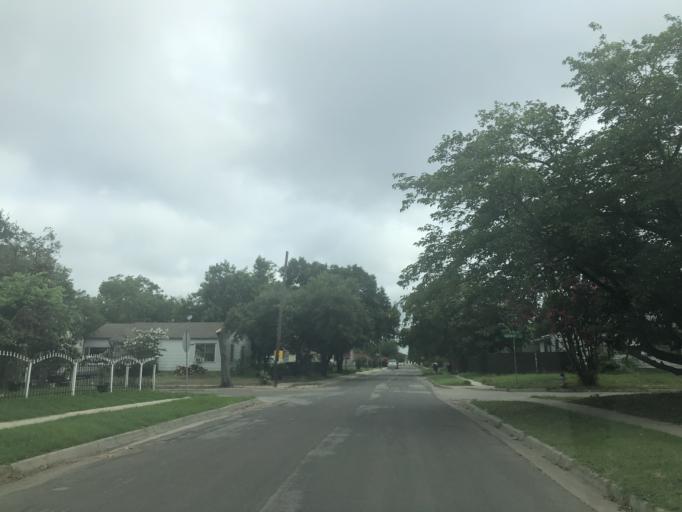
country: US
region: Texas
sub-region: Dallas County
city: University Park
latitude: 32.8700
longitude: -96.8588
